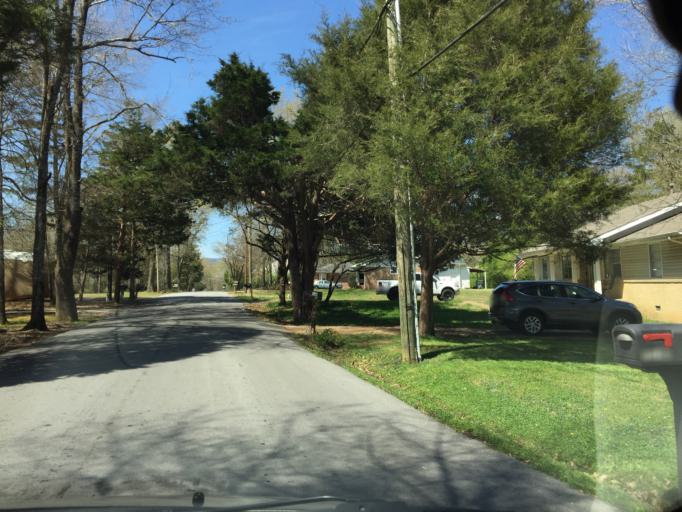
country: US
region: Tennessee
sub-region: Hamilton County
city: Middle Valley
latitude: 35.1607
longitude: -85.2101
